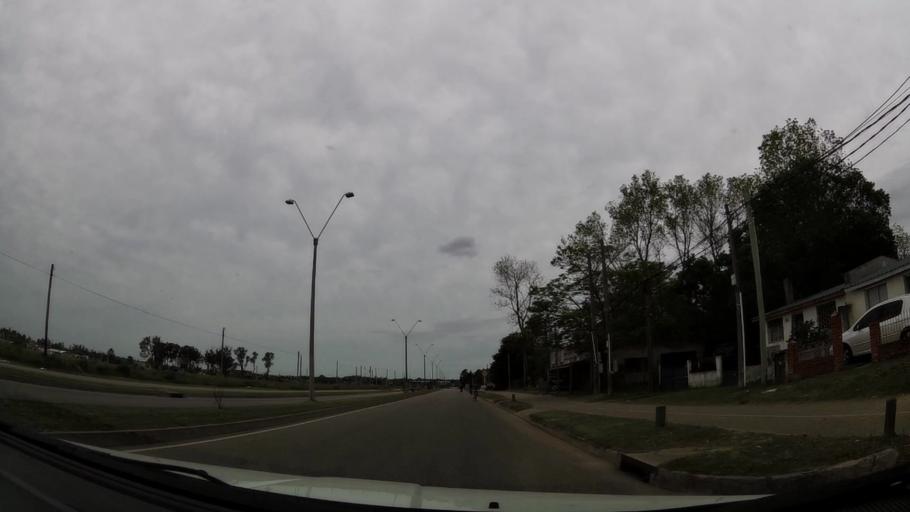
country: UY
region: Maldonado
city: Maldonado
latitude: -34.8883
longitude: -54.9652
